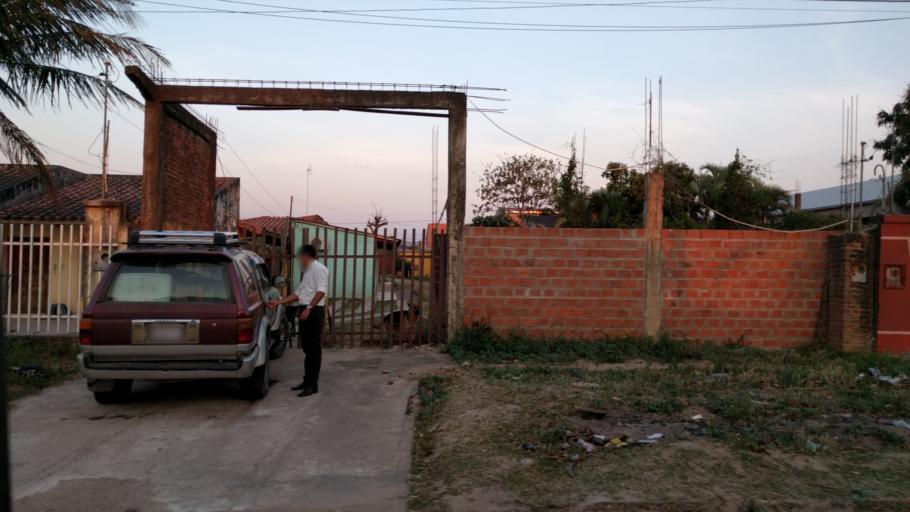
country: BO
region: Santa Cruz
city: Santa Cruz de la Sierra
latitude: -17.7527
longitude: -63.1497
